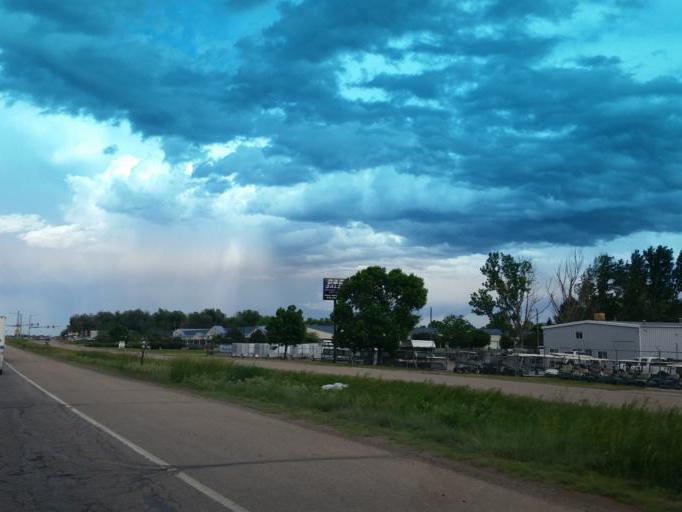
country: US
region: Colorado
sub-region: Larimer County
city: Fort Collins
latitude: 40.5810
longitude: -105.0314
